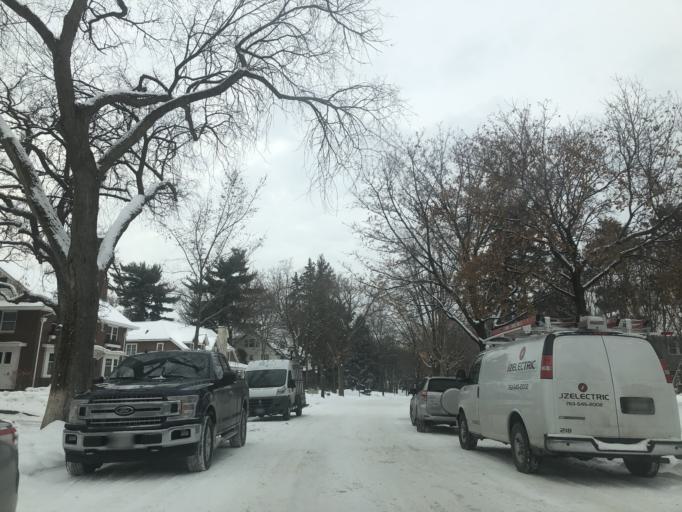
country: US
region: Minnesota
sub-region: Hennepin County
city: Richfield
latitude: 44.9212
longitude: -93.2953
